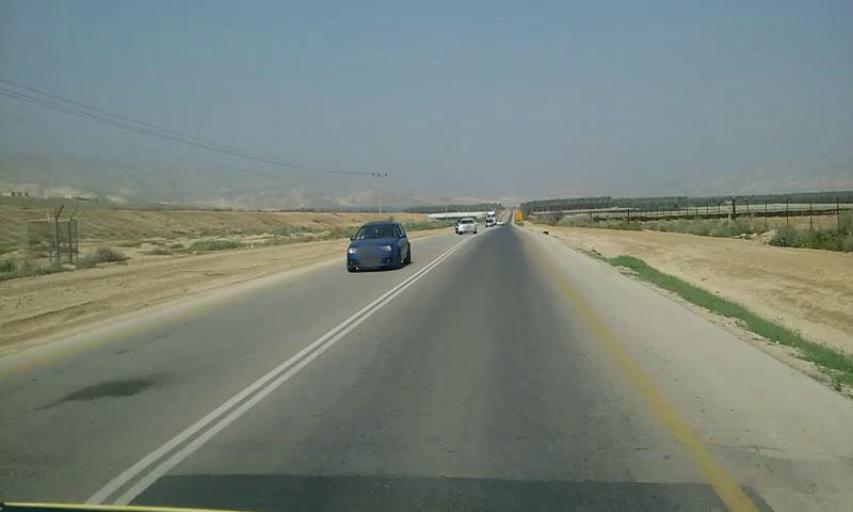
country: PS
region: West Bank
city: Al `Awja
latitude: 31.9864
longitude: 35.4621
